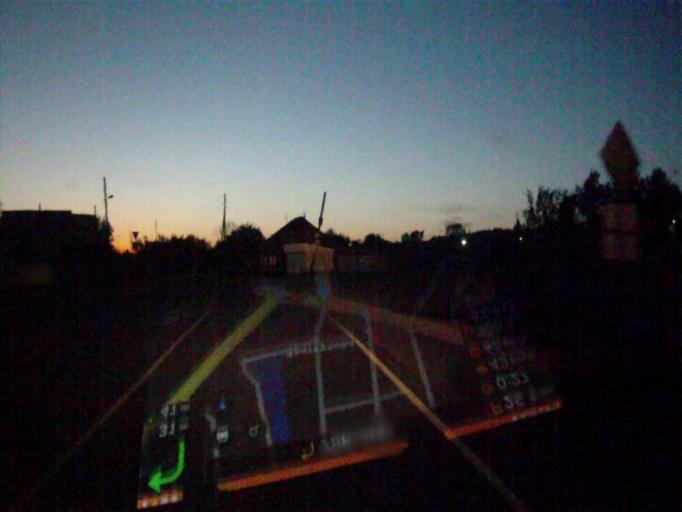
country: RU
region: Chelyabinsk
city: Chebarkul'
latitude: 55.2289
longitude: 60.4525
